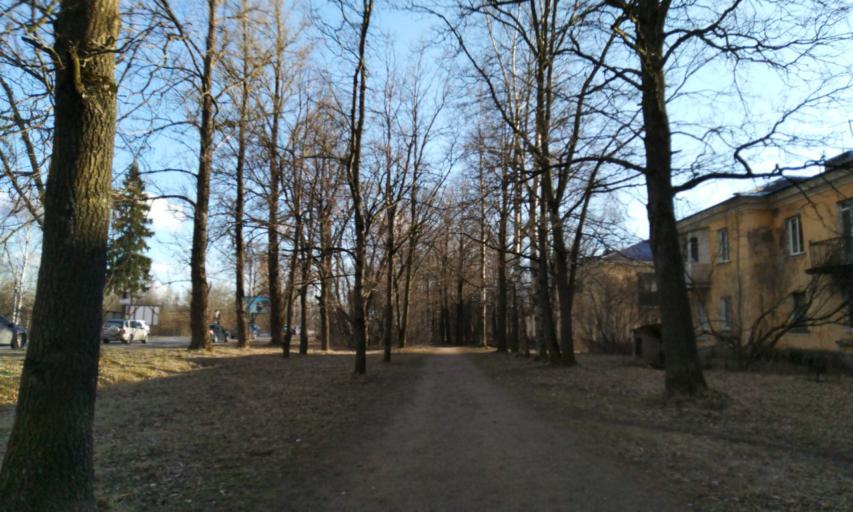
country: RU
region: Leningrad
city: Toksovo
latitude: 60.1104
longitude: 30.5008
